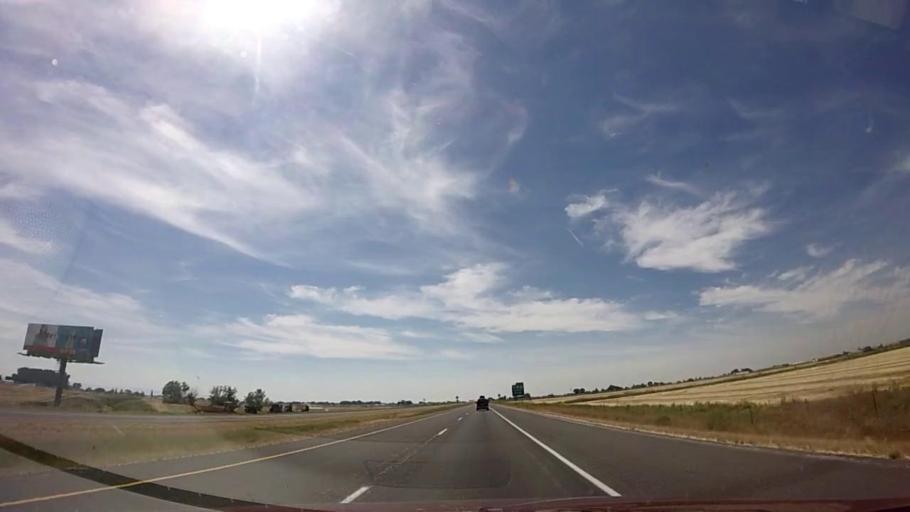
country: US
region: Idaho
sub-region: Minidoka County
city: Heyburn
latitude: 42.5691
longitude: -113.7092
